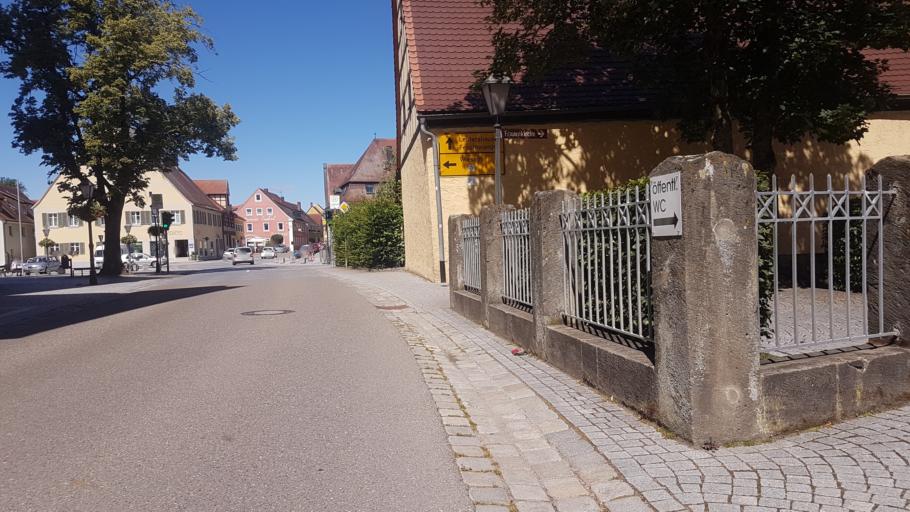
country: DE
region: Bavaria
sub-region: Regierungsbezirk Mittelfranken
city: Herrieden
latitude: 49.2328
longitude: 10.4985
